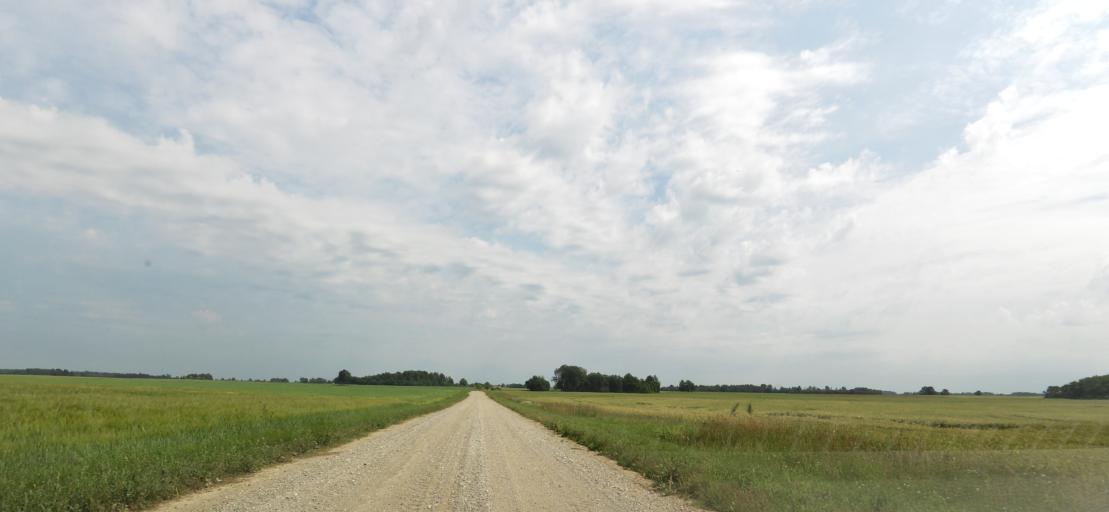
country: LT
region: Panevezys
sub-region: Birzai
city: Birzai
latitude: 56.3187
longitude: 24.6843
